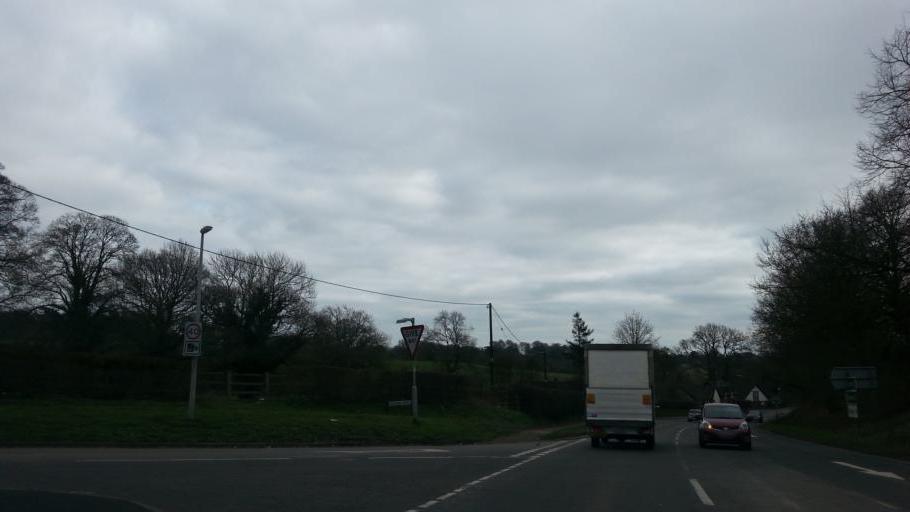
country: GB
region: England
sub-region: Staffordshire
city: Stafford
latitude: 52.8662
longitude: -2.0813
